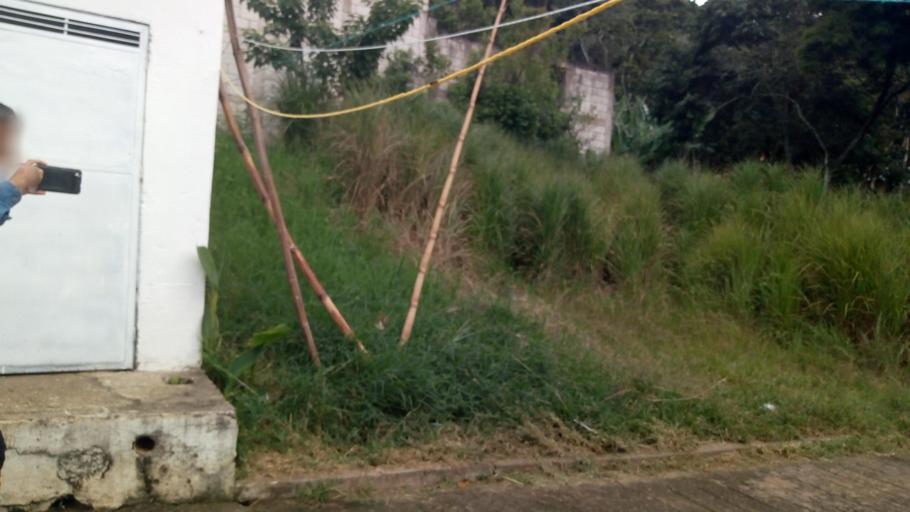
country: GT
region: Guatemala
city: Villa Canales
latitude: 14.5081
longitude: -90.5175
